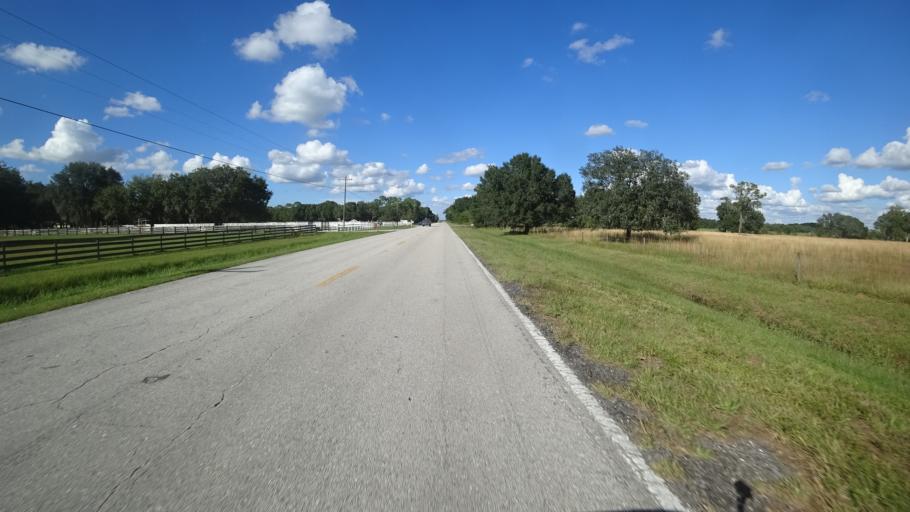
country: US
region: Florida
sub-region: Sarasota County
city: The Meadows
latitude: 27.4553
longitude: -82.3033
